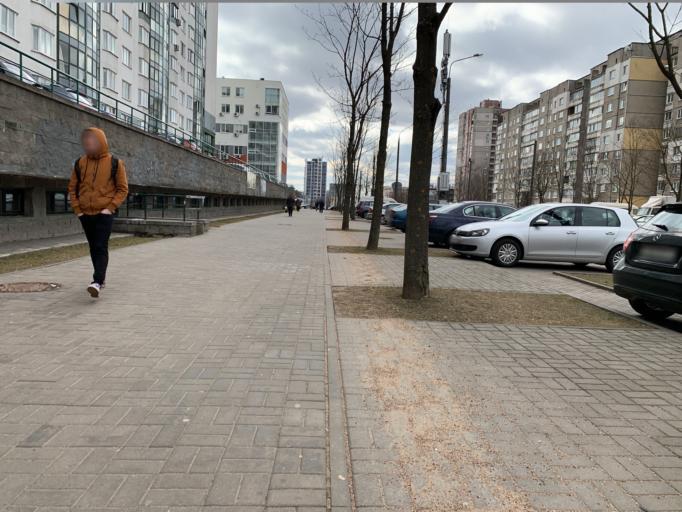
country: BY
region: Minsk
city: Minsk
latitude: 53.9309
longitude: 27.5883
